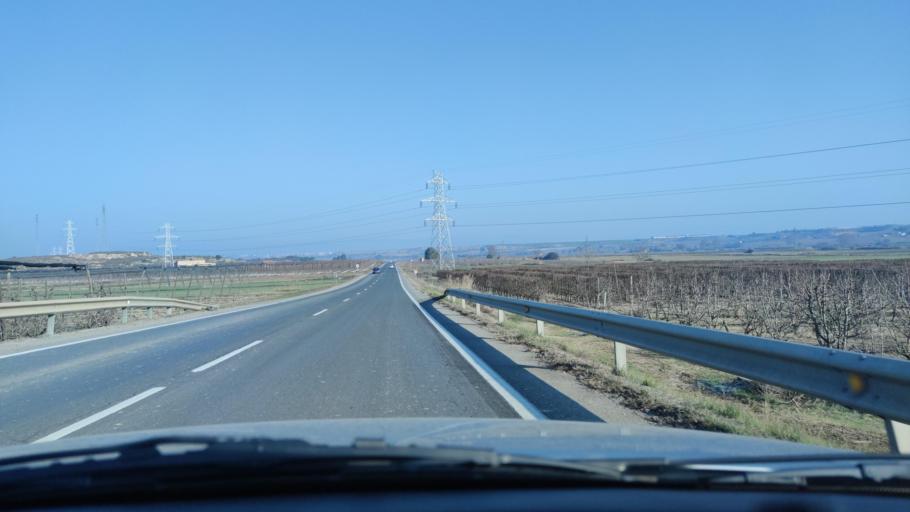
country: ES
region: Catalonia
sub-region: Provincia de Lleida
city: Torrefarrera
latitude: 41.7041
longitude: 0.6368
